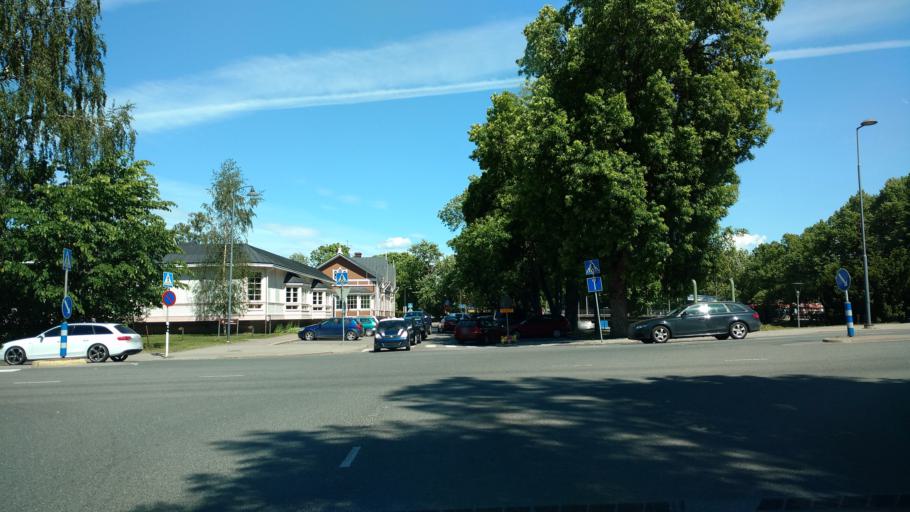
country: FI
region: Varsinais-Suomi
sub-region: Salo
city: Salo
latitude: 60.3844
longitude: 23.1258
